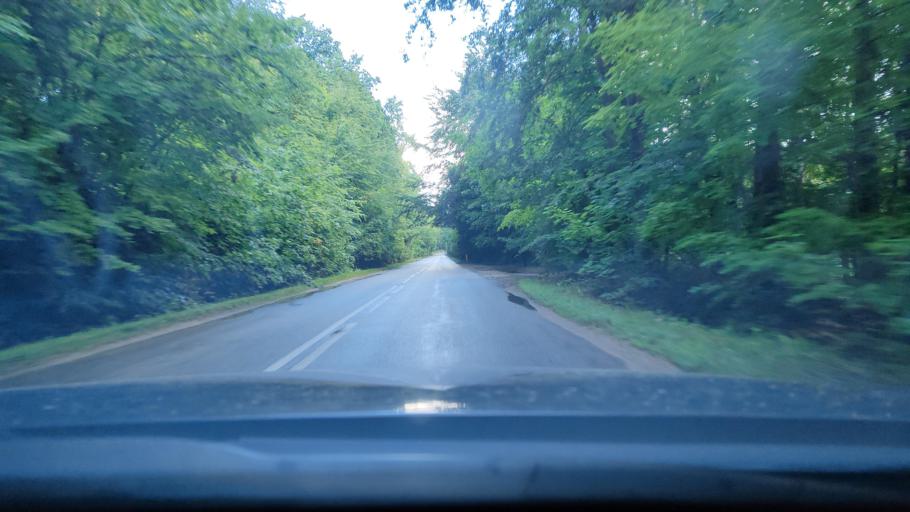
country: PL
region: Pomeranian Voivodeship
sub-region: Powiat pucki
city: Krokowa
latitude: 54.7153
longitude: 18.1658
